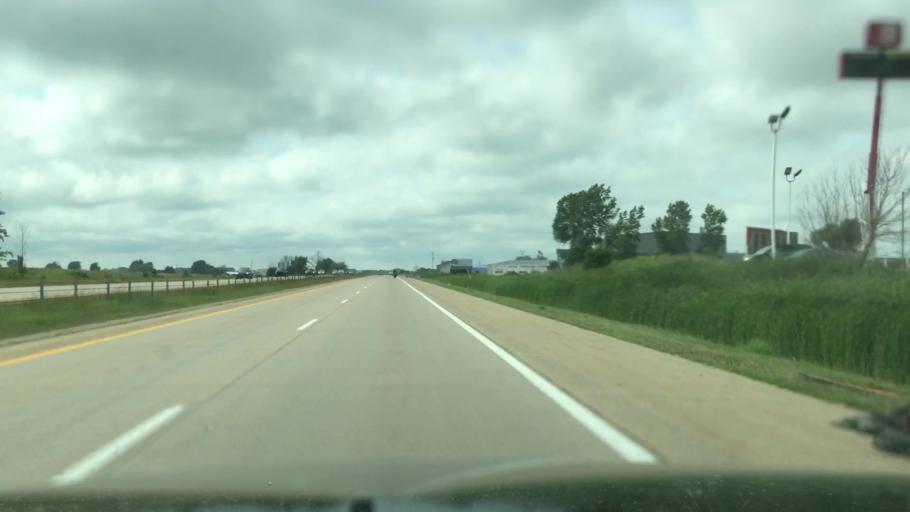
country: US
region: Michigan
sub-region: Ottawa County
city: Coopersville
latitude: 43.0569
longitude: -85.9577
